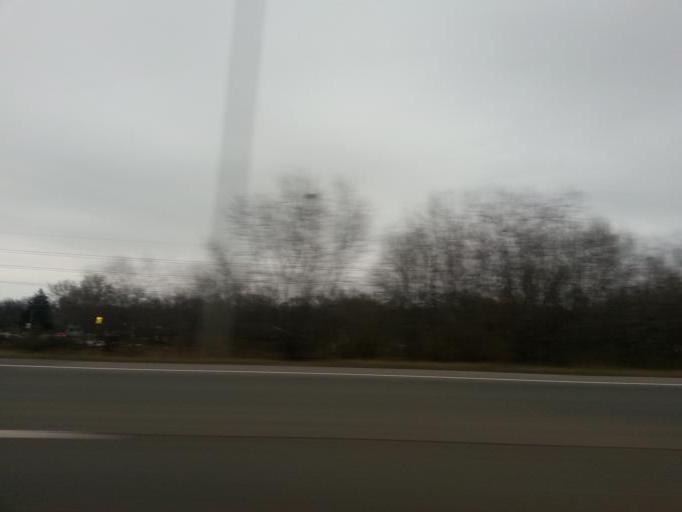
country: US
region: Iowa
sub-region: Linn County
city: Cedar Rapids
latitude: 42.0172
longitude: -91.6666
